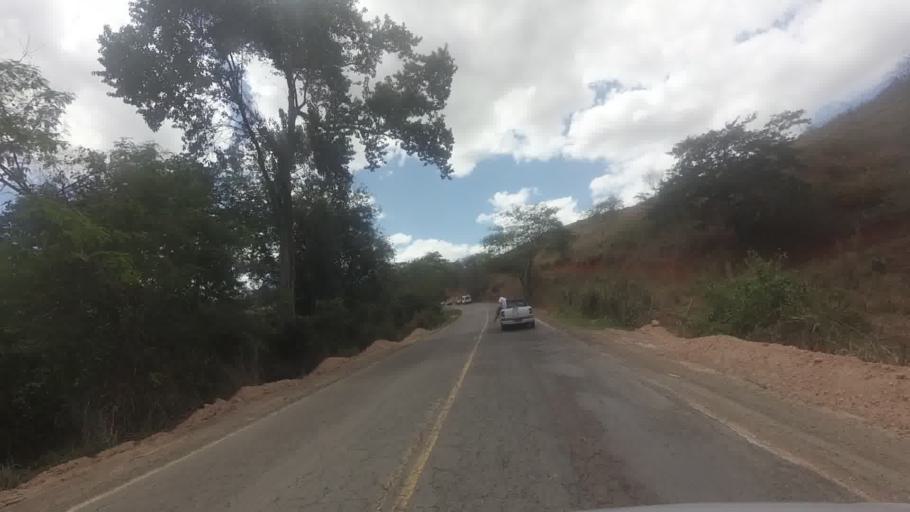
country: BR
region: Rio de Janeiro
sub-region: Santo Antonio De Padua
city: Santo Antonio de Padua
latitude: -21.5217
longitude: -42.1052
